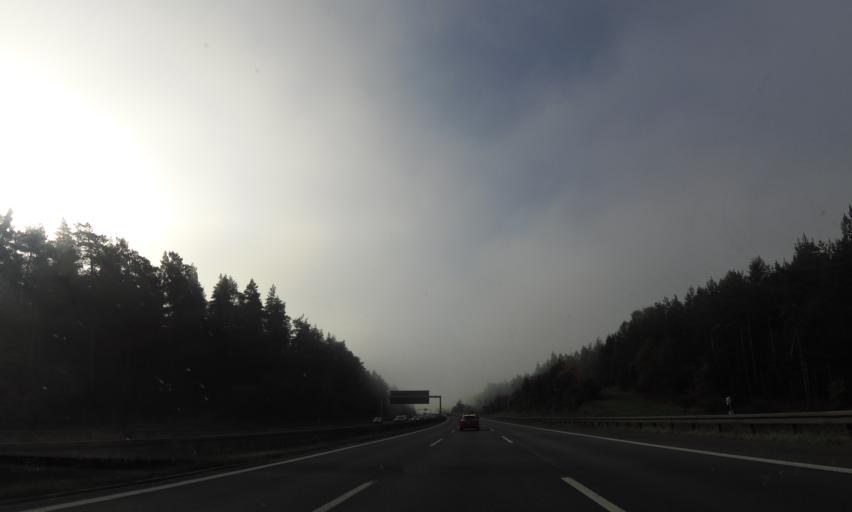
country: DE
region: Bavaria
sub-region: Upper Franconia
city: Pottenstein
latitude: 49.6996
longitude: 11.4650
